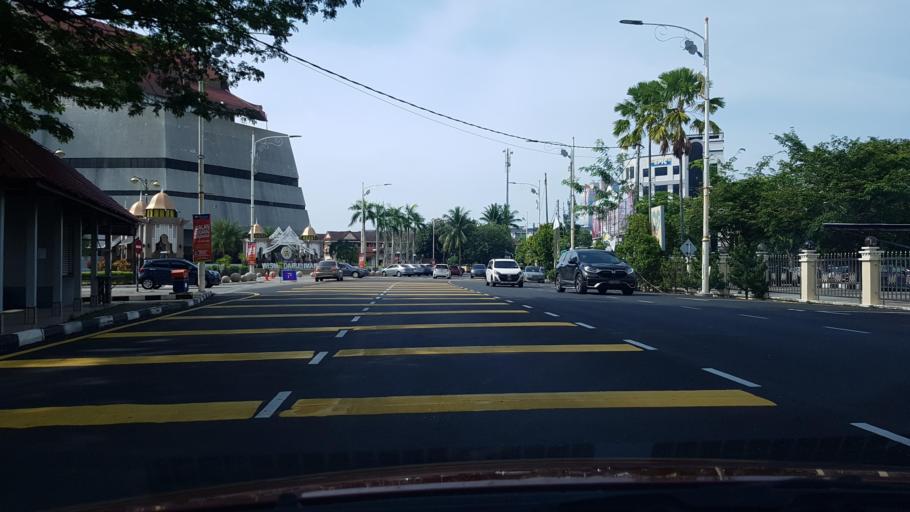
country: MY
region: Terengganu
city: Kuala Terengganu
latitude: 5.3293
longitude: 103.1414
